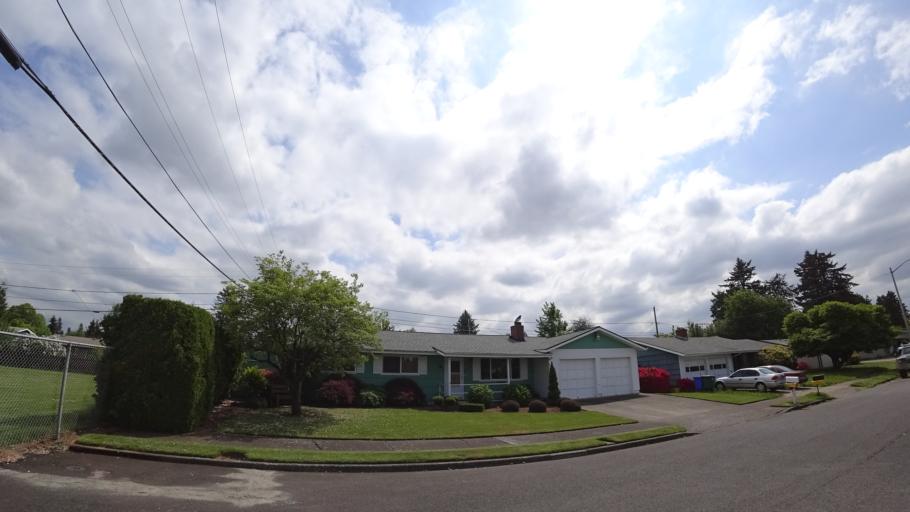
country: US
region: Oregon
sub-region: Multnomah County
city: Fairview
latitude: 45.5159
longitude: -122.4875
